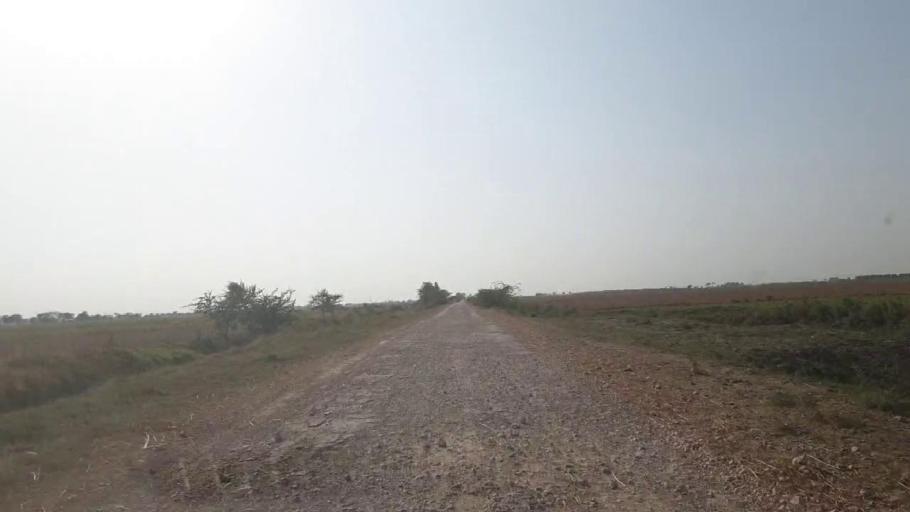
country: PK
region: Sindh
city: Kario
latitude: 24.5765
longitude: 68.5140
